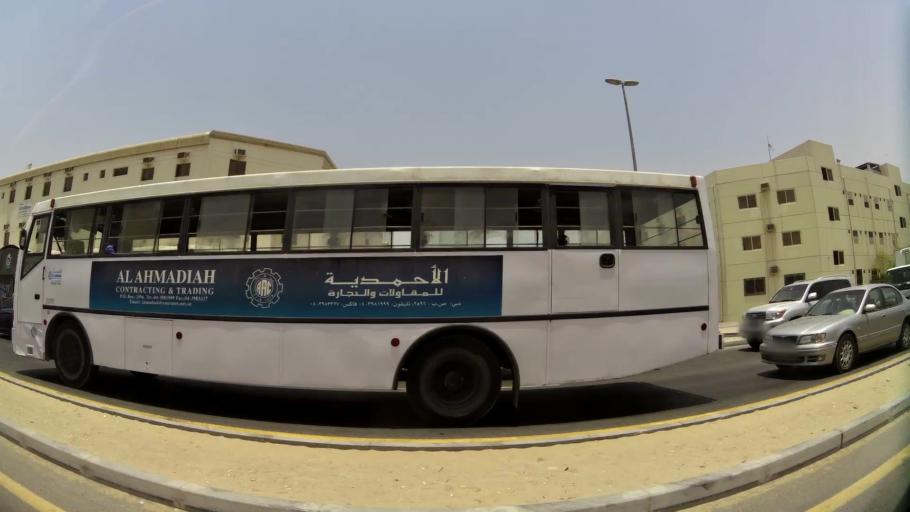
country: AE
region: Ash Shariqah
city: Sharjah
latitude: 25.2707
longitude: 55.4294
